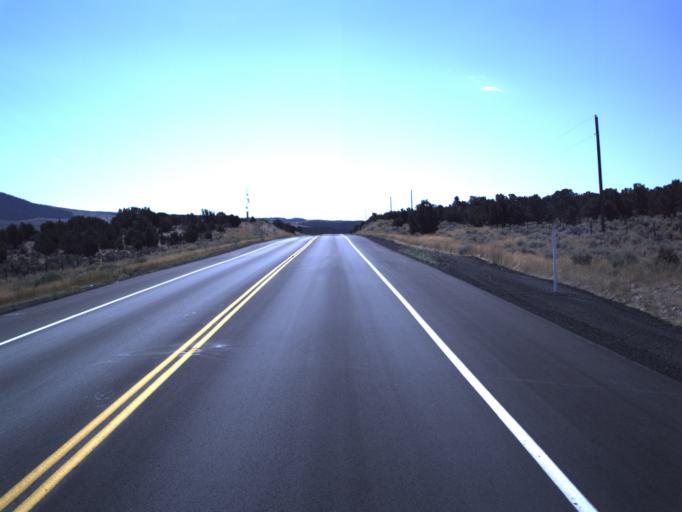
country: US
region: Utah
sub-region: Utah County
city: Eagle Mountain
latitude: 40.0365
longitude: -112.2875
